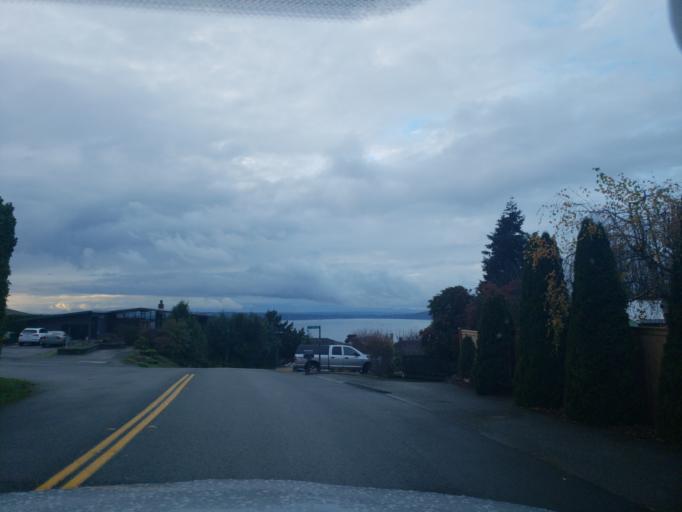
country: US
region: Washington
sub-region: King County
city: Shoreline
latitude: 47.7568
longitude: -122.3742
